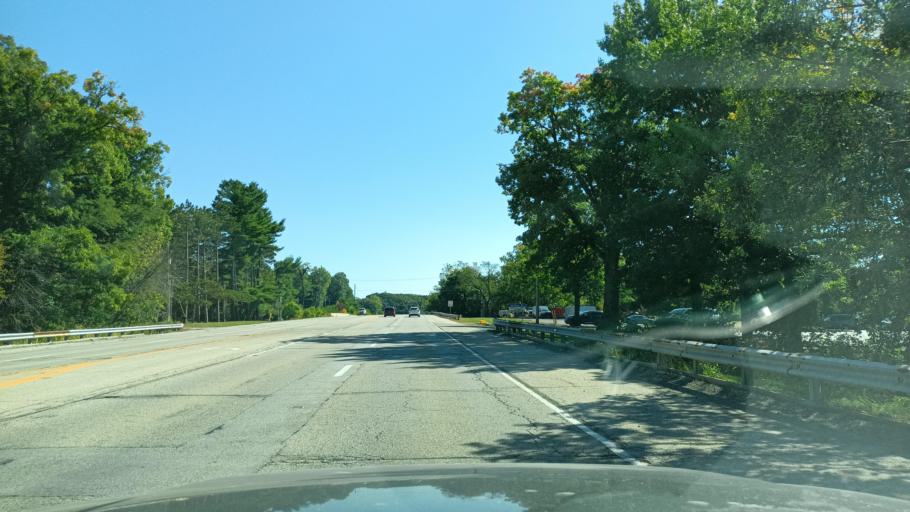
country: US
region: Illinois
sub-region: Peoria County
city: West Peoria
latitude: 40.7697
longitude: -89.6518
